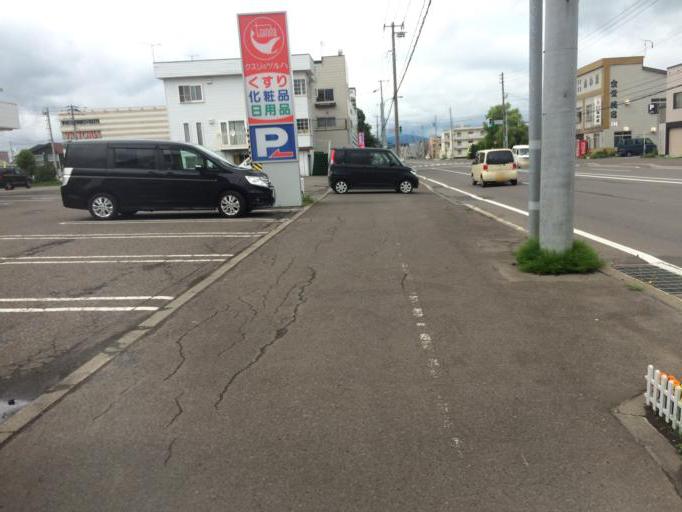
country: JP
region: Hokkaido
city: Niseko Town
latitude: 42.8956
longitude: 140.7519
